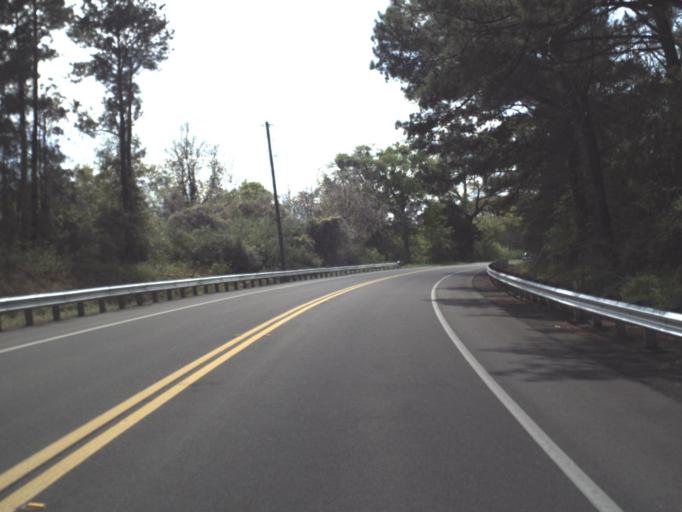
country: US
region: Alabama
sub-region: Covington County
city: Florala
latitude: 30.9636
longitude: -86.4246
